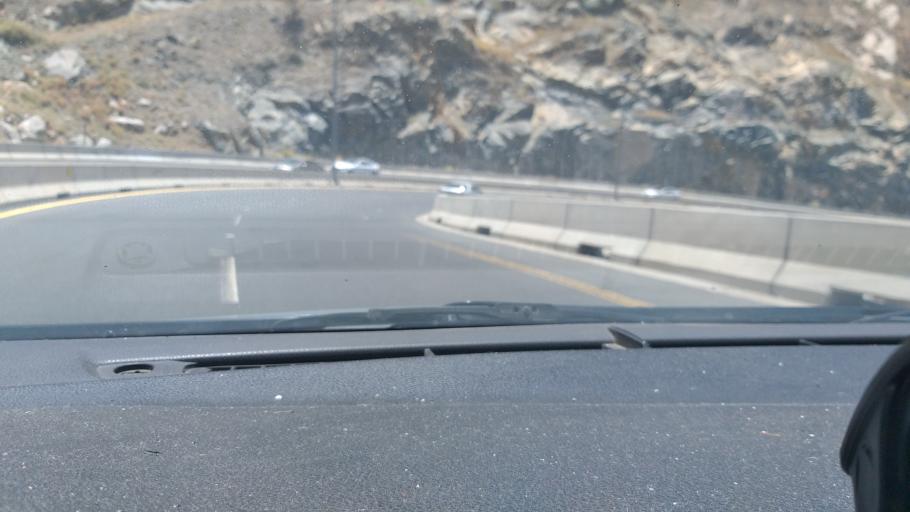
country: SA
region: Makkah
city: Al Hada
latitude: 21.3548
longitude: 40.2587
